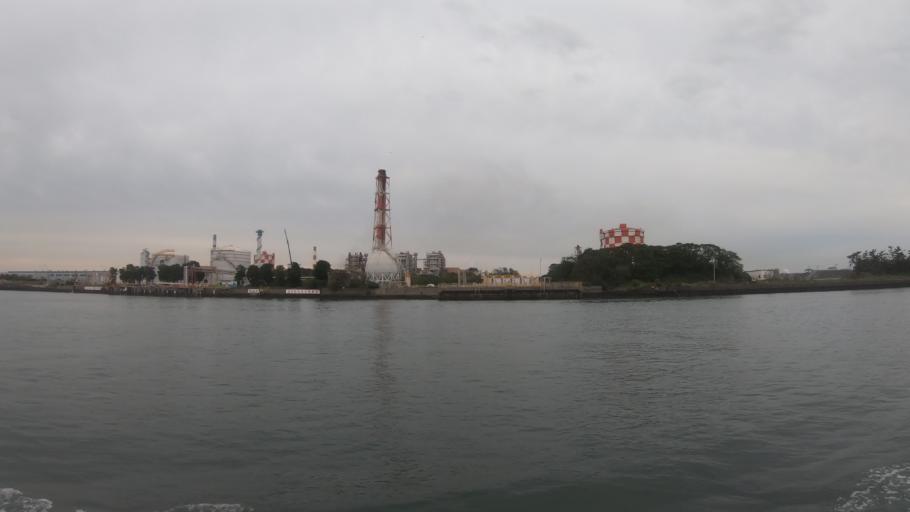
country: JP
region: Kanagawa
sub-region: Kawasaki-shi
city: Kawasaki
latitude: 35.4873
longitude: 139.7139
